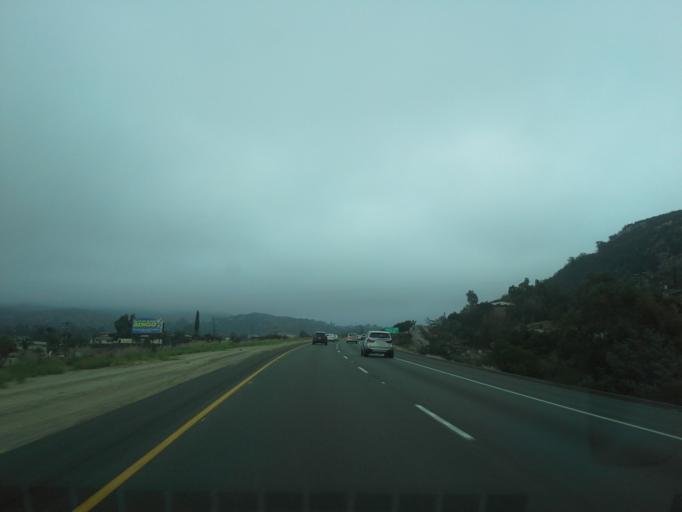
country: US
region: California
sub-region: San Diego County
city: Harbison Canyon
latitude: 32.8556
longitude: -116.8332
